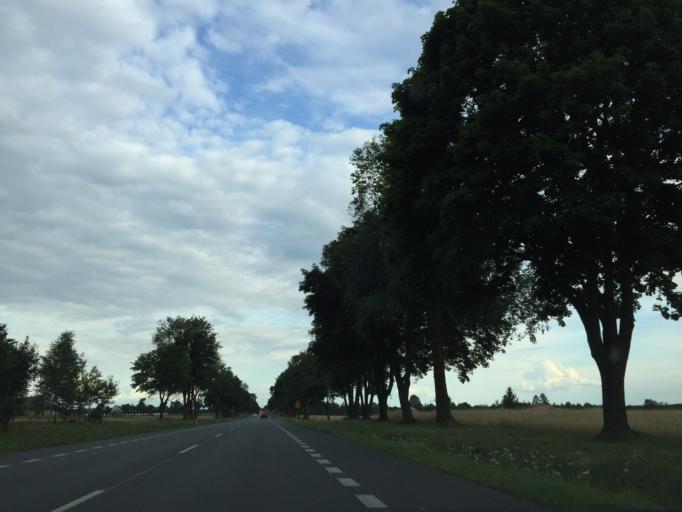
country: PL
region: Lublin Voivodeship
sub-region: Powiat lubartowski
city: Firlej
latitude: 51.5869
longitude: 22.4844
